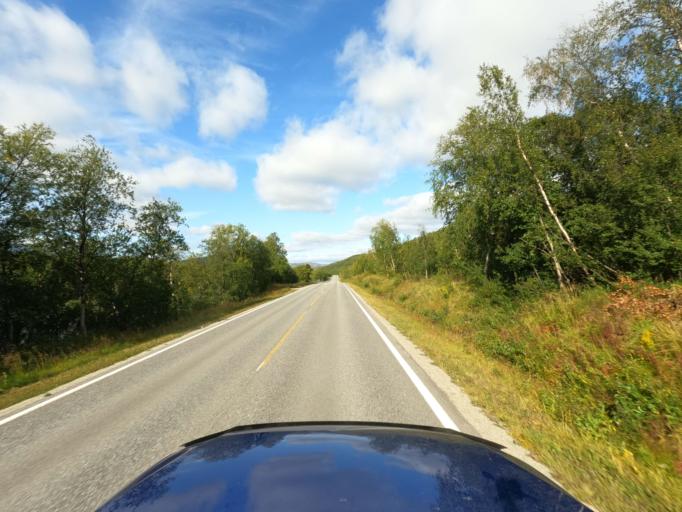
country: NO
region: Finnmark Fylke
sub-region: Porsanger
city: Lakselv
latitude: 69.9321
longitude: 24.9778
